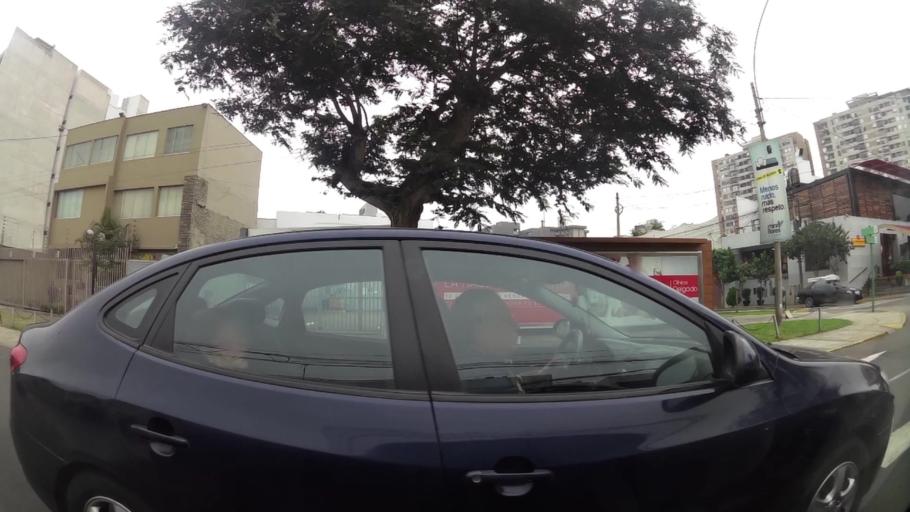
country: PE
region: Lima
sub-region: Lima
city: Surco
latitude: -12.1301
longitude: -77.0246
